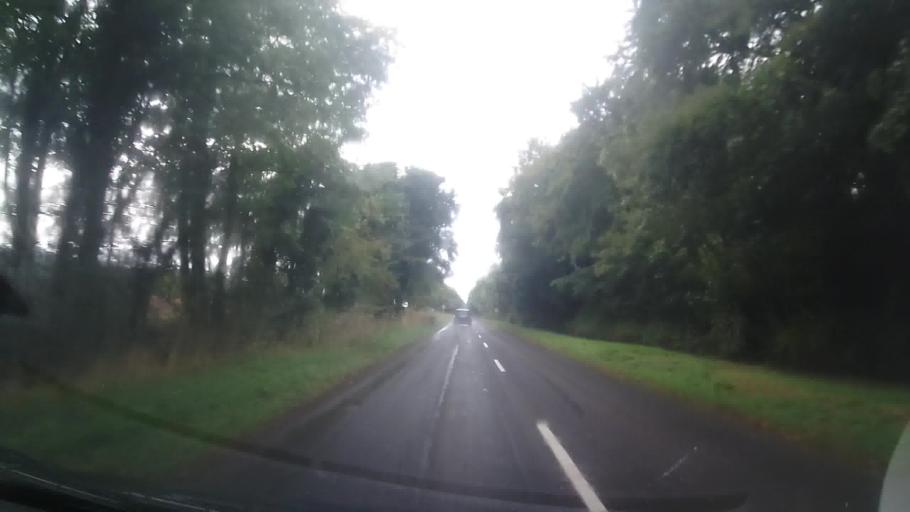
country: GB
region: England
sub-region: Oxfordshire
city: Woodstock
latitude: 51.8675
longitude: -1.3891
